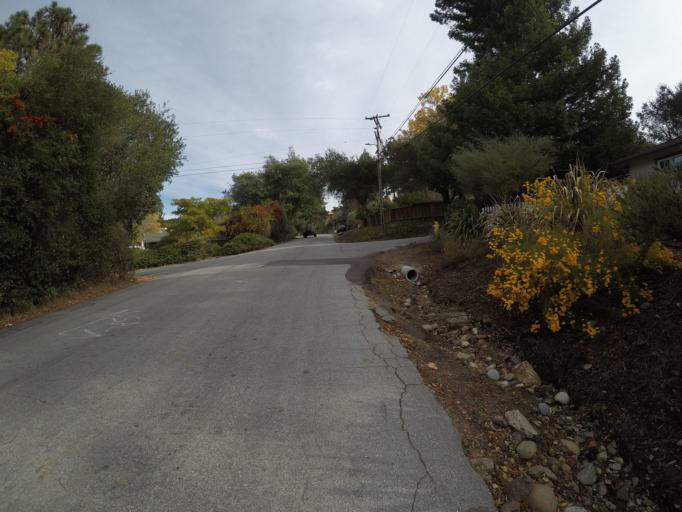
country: US
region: California
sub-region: Santa Cruz County
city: Scotts Valley
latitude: 37.0579
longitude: -121.9980
